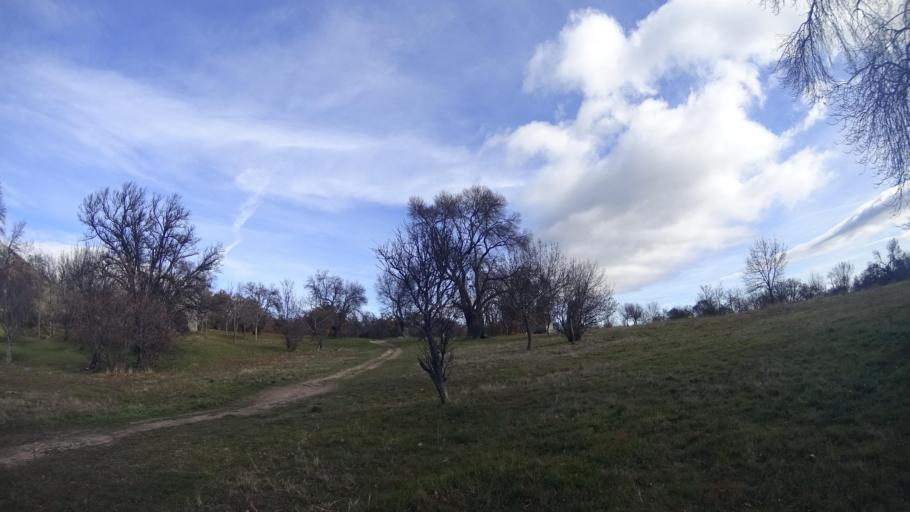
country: ES
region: Madrid
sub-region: Provincia de Madrid
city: San Lorenzo de El Escorial
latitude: 40.5819
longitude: -4.1461
